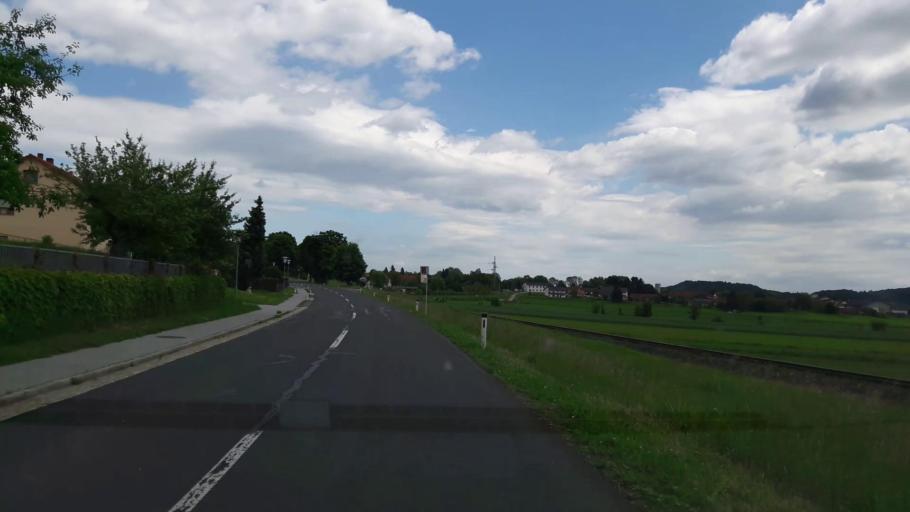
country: AT
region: Styria
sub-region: Politischer Bezirk Hartberg-Fuerstenfeld
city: UEbersbach
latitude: 47.0282
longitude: 16.0417
